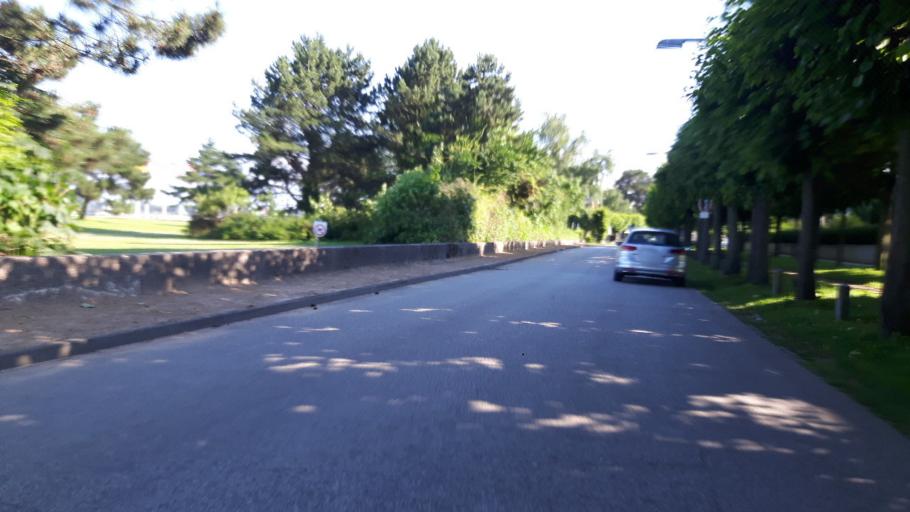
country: DE
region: Schleswig-Holstein
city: Travemuende
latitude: 53.9712
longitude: 10.8814
